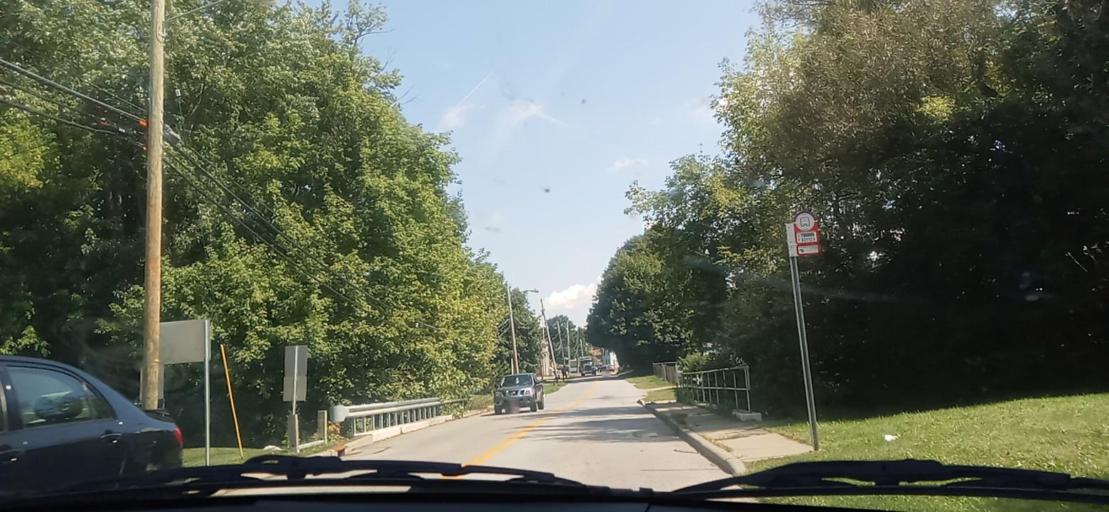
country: US
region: Ohio
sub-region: Summit County
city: Barberton
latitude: 41.0386
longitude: -81.5783
